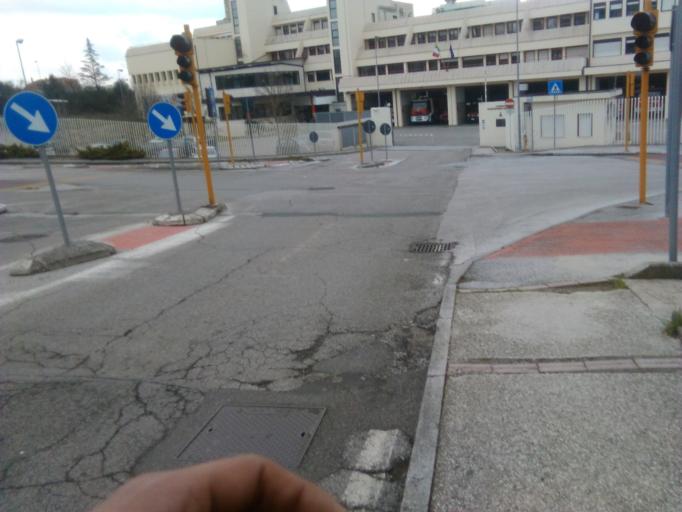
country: IT
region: Umbria
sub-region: Provincia di Perugia
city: Lacugnano
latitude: 43.0918
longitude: 12.3632
